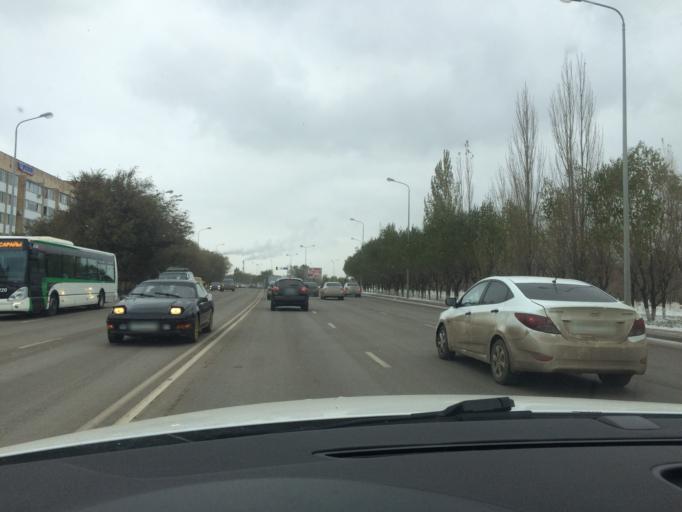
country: KZ
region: Astana Qalasy
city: Astana
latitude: 51.1640
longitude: 71.4729
